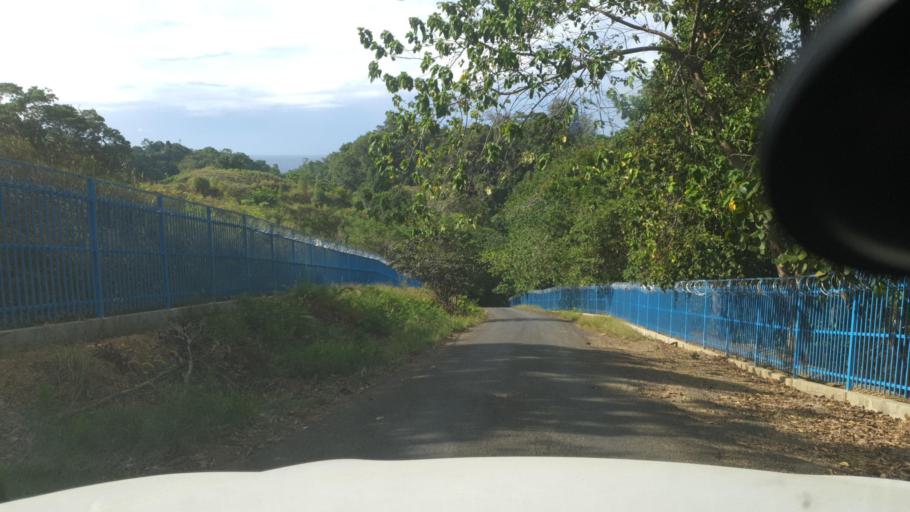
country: SB
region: Guadalcanal
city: Honiara
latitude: -9.4405
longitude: 159.9385
